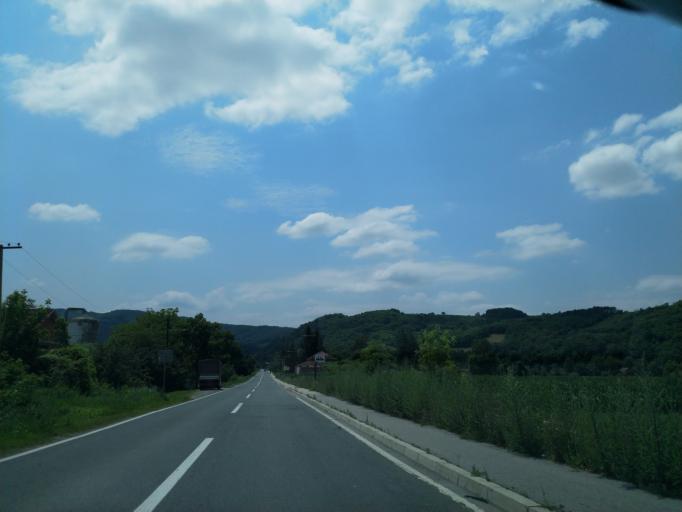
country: RS
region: Central Serbia
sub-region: Toplicki Okrug
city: Blace
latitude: 43.4303
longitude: 21.2081
